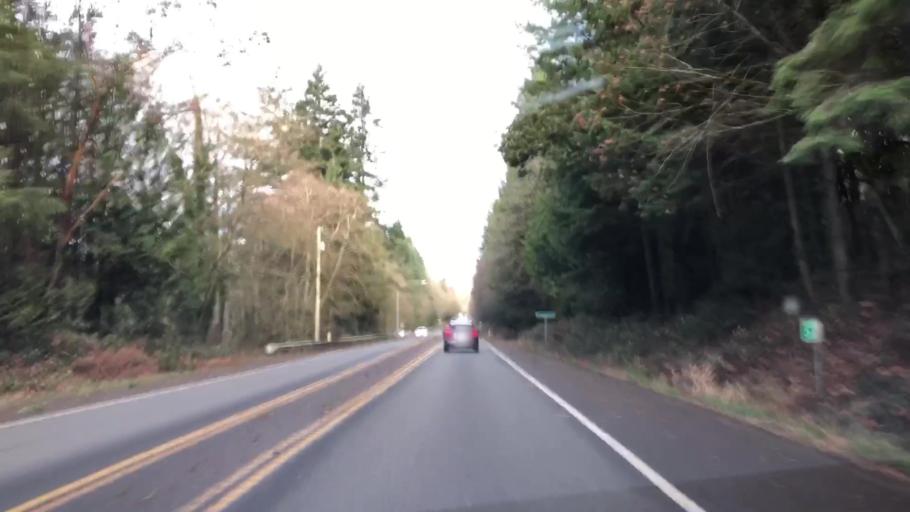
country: US
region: Washington
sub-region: Kitsap County
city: Bainbridge Island
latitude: 47.6632
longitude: -122.5257
